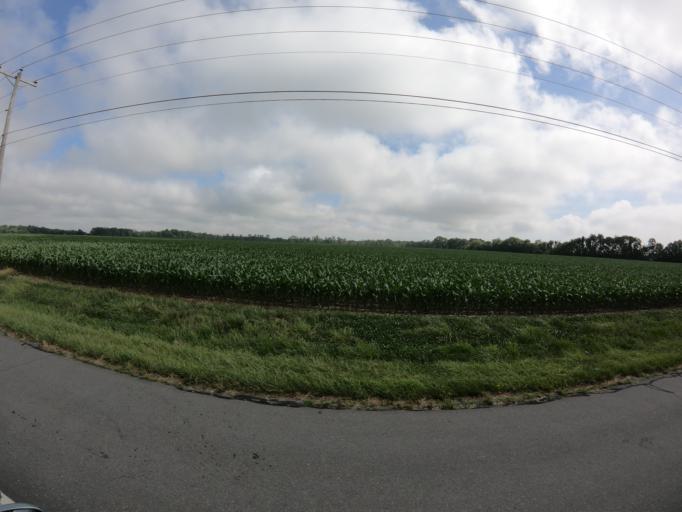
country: US
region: Delaware
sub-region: Kent County
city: Riverview
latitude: 39.0118
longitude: -75.4892
